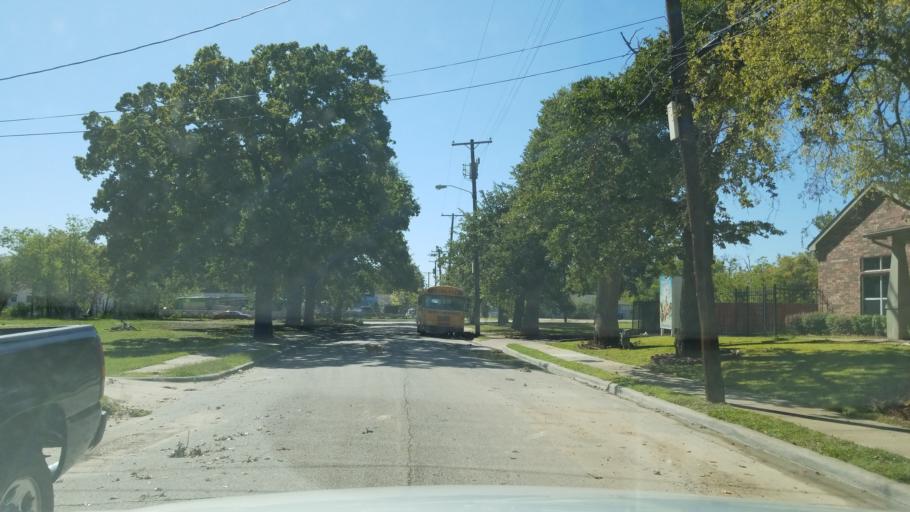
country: US
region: Texas
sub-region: Dallas County
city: Dallas
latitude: 32.7786
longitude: -96.7470
